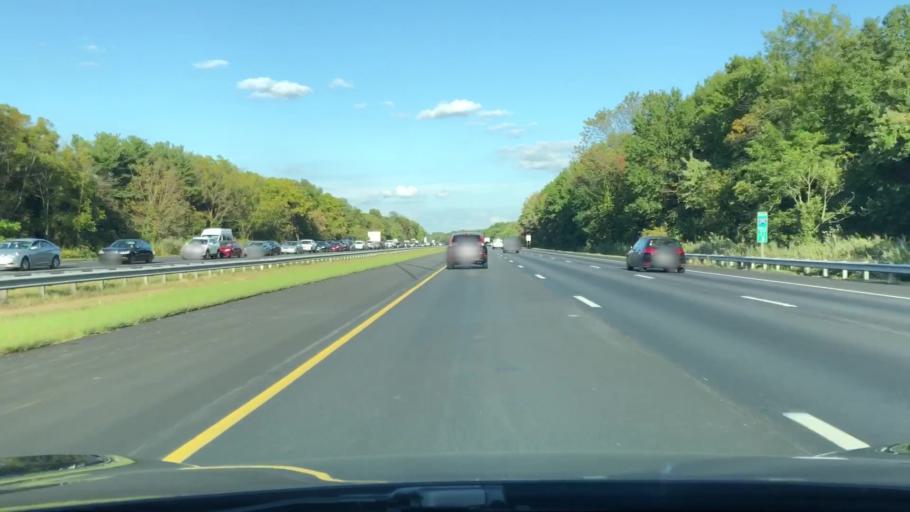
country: US
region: New Jersey
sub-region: Burlington County
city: Ramblewood
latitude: 39.9410
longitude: -74.9505
